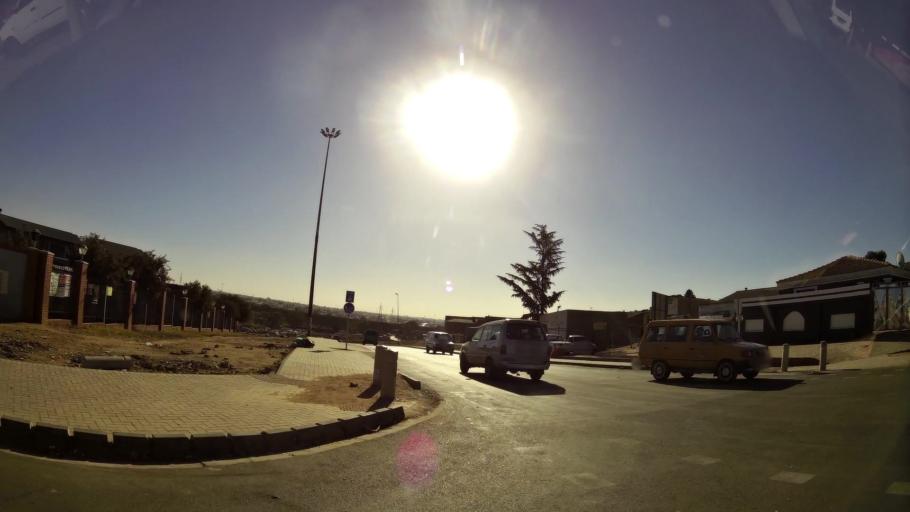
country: ZA
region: Gauteng
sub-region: Ekurhuleni Metropolitan Municipality
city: Tembisa
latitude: -26.0258
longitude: 28.2096
